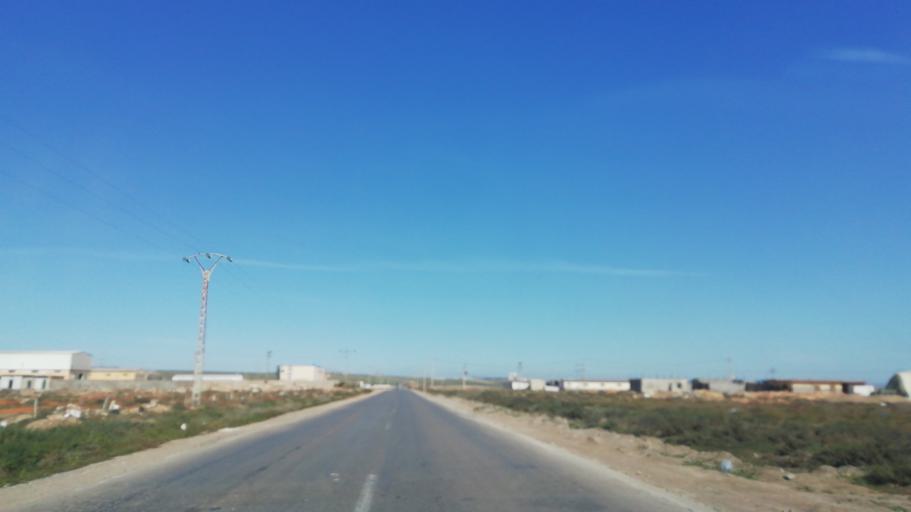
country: DZ
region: Oran
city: Es Senia
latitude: 35.5190
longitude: -0.5885
